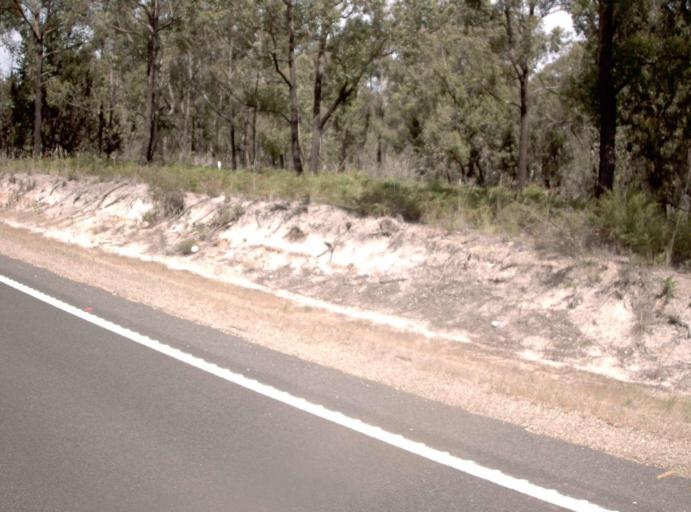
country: AU
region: Victoria
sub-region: Wellington
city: Sale
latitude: -37.9159
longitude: 147.2951
